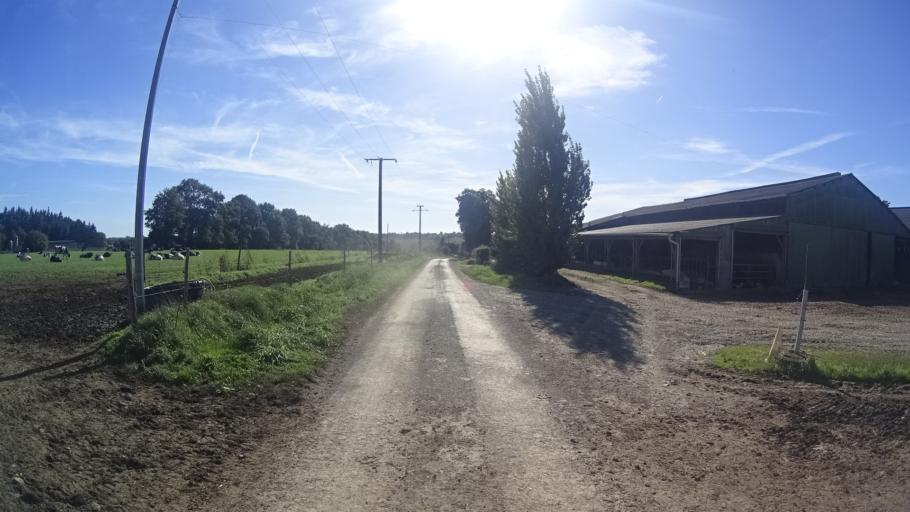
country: FR
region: Brittany
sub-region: Departement du Morbihan
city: Saint-Vincent-sur-Oust
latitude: 47.7335
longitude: -2.1732
